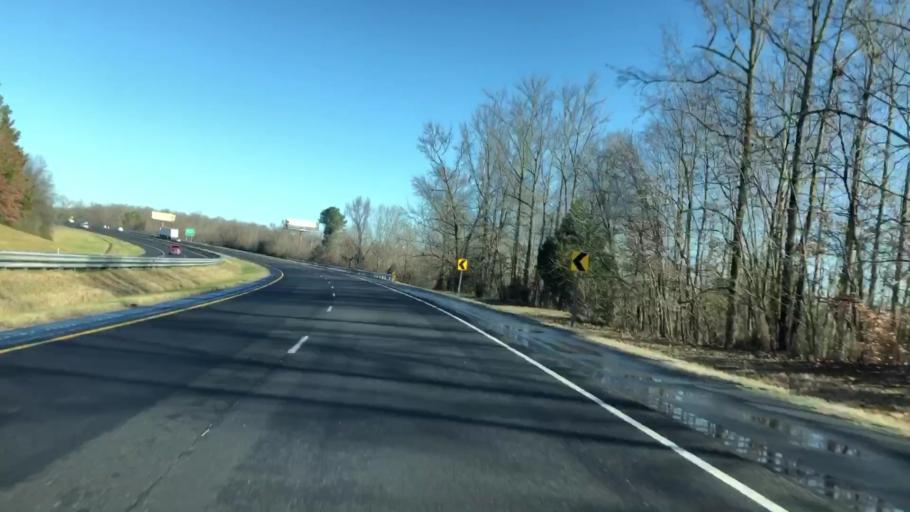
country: US
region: Alabama
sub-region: Limestone County
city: Ardmore
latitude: 34.8998
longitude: -86.9069
